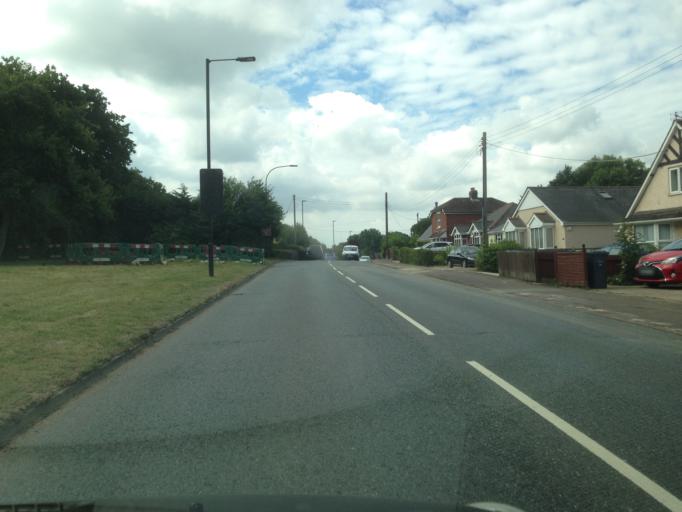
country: GB
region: England
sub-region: Isle of Wight
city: Newport
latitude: 50.7107
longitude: -1.2807
